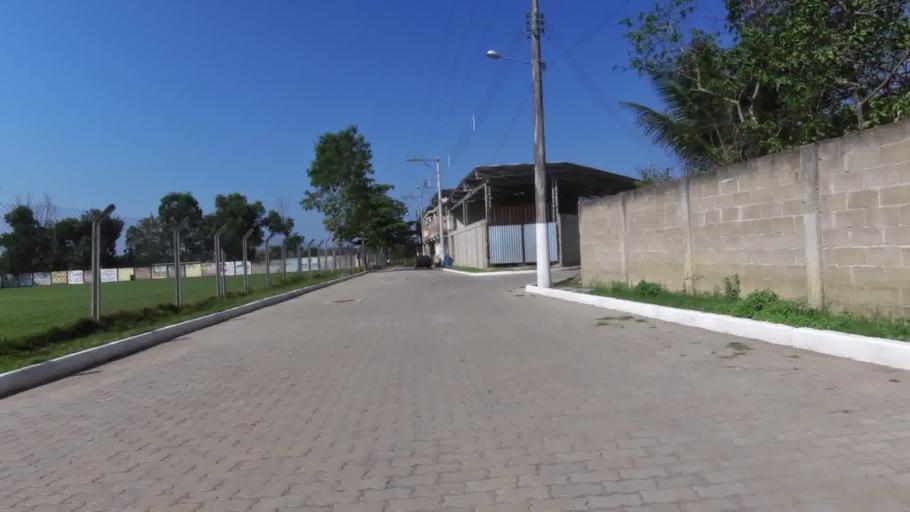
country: BR
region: Espirito Santo
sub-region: Piuma
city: Piuma
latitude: -20.8098
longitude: -40.7375
